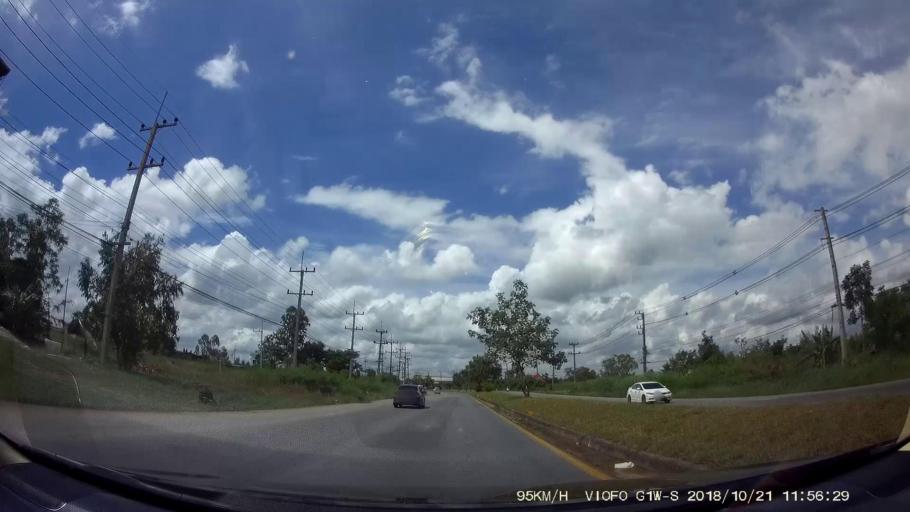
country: TH
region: Chaiyaphum
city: Chatturat
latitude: 15.5789
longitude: 101.8750
